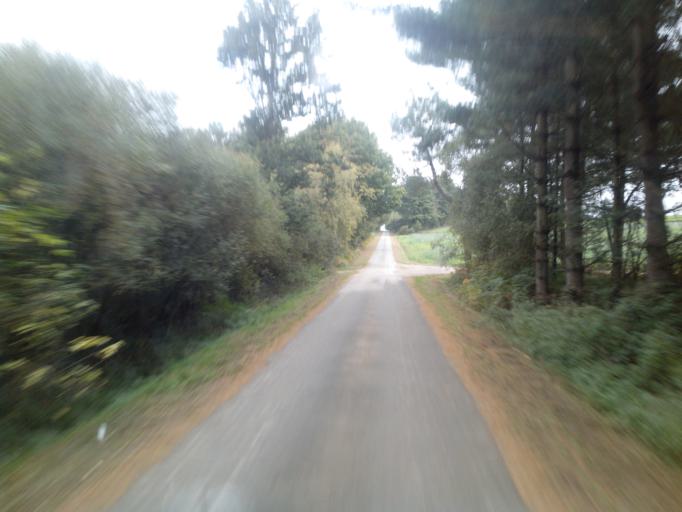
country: FR
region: Brittany
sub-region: Departement du Morbihan
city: Mauron
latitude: 48.0618
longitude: -2.3257
